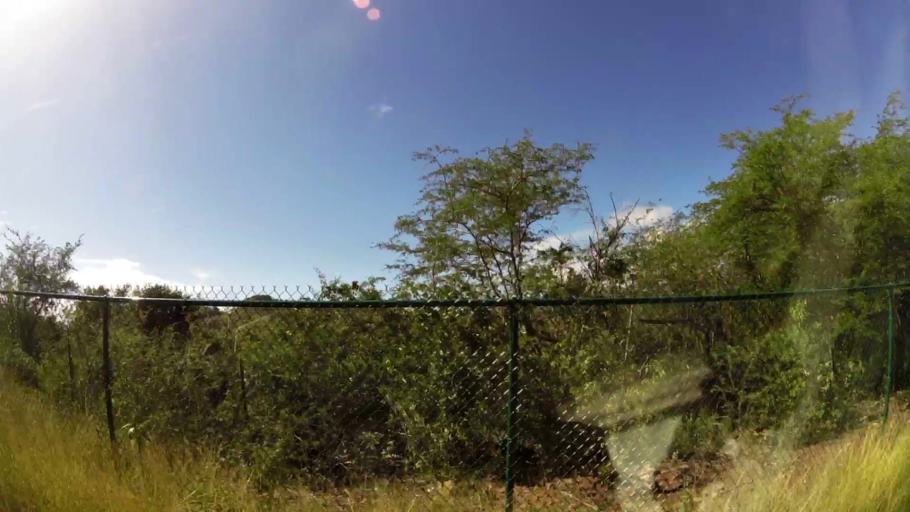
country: AG
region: Saint Paul
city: Falmouth
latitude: 17.0092
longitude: -61.7613
